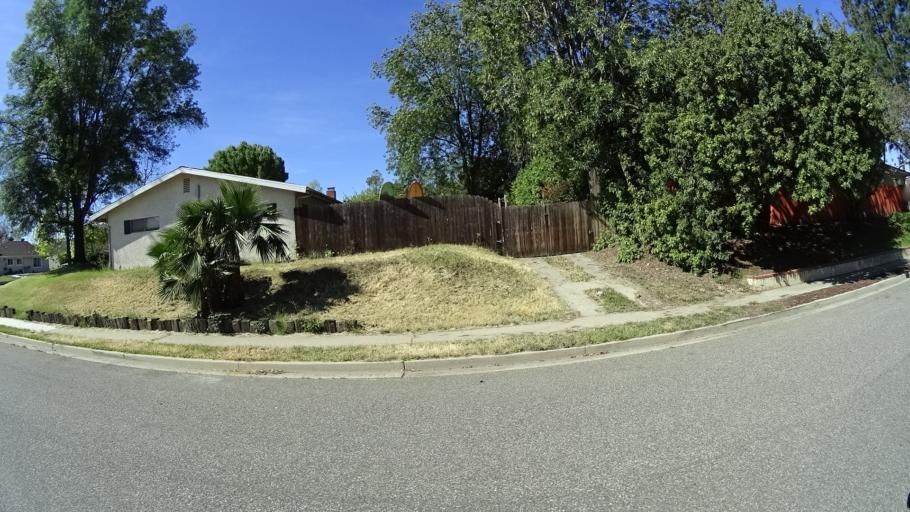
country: US
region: California
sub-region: Ventura County
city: Thousand Oaks
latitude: 34.2255
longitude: -118.8604
